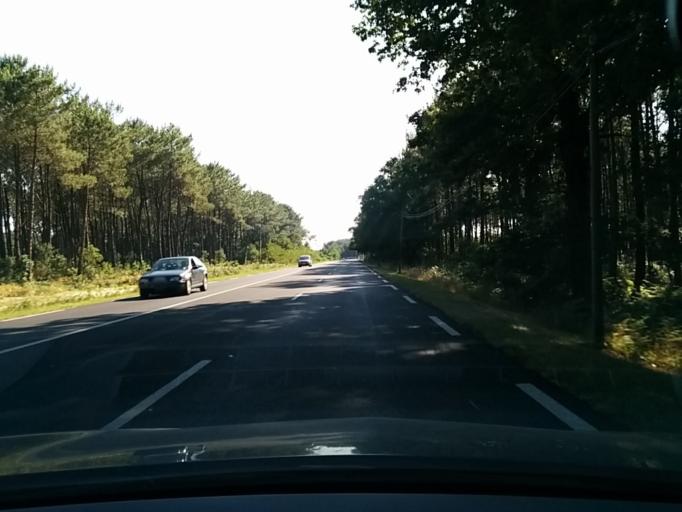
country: FR
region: Aquitaine
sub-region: Departement des Landes
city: Labenne
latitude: 43.6169
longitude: -1.3952
